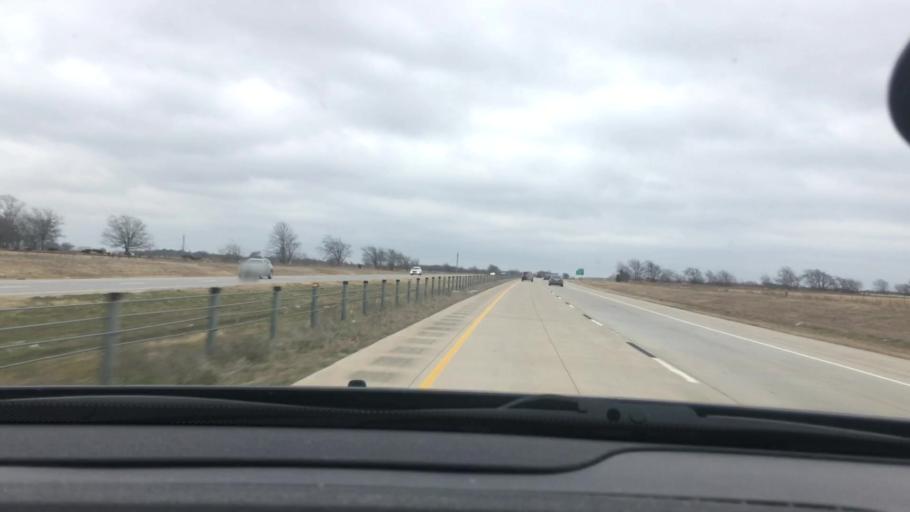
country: US
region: Oklahoma
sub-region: Bryan County
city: Durant
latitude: 34.0822
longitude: -96.3341
